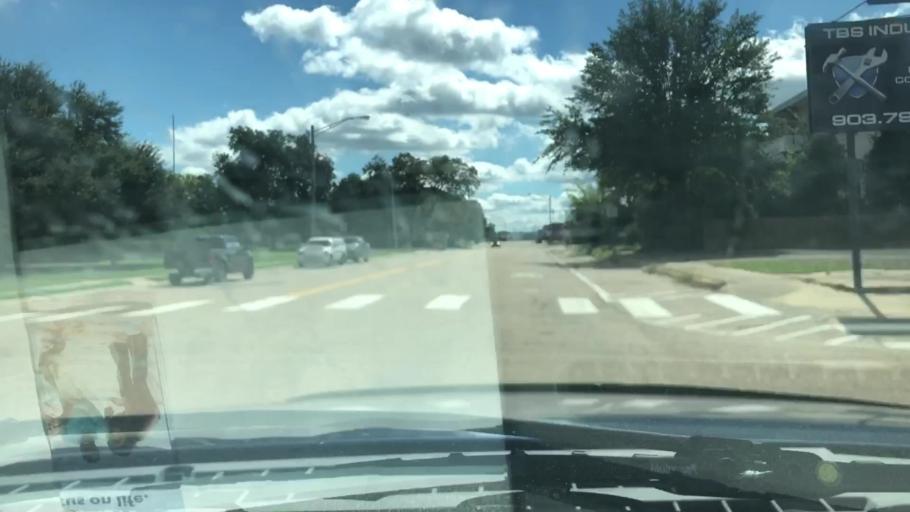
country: US
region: Texas
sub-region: Bowie County
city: Texarkana
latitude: 33.4242
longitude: -94.0475
